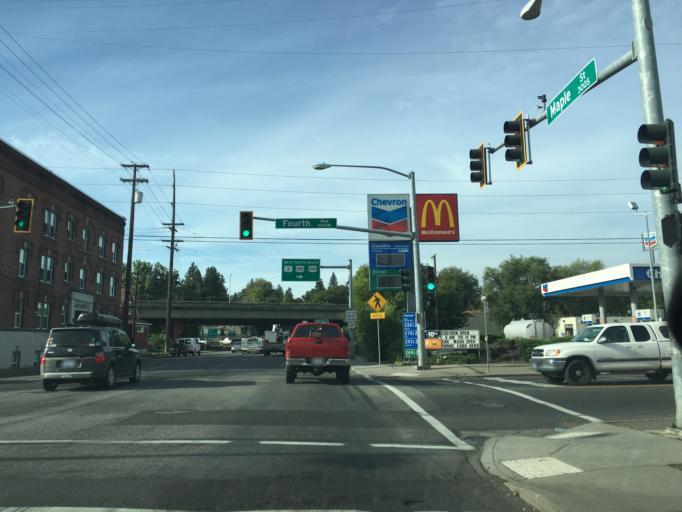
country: US
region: Washington
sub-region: Spokane County
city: Spokane
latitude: 47.6527
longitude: -117.4357
